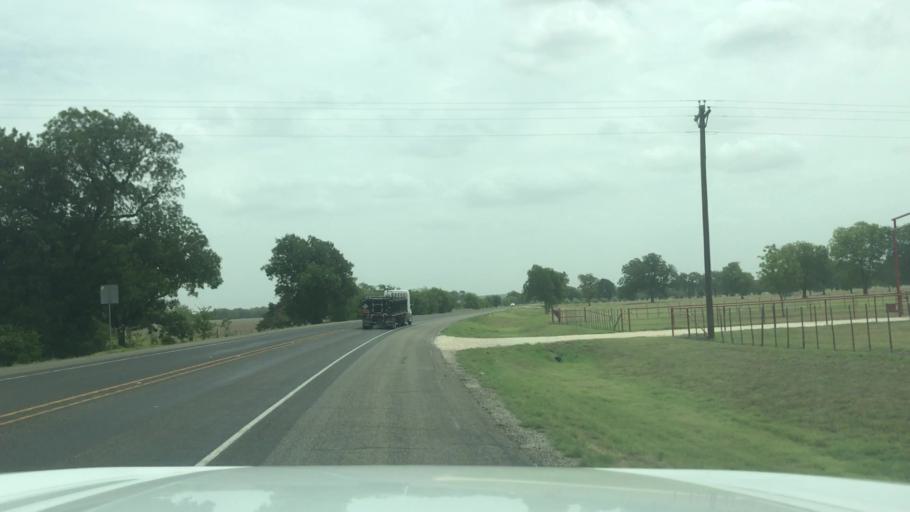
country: US
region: Texas
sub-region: Bosque County
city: Valley Mills
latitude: 31.6746
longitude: -97.5098
